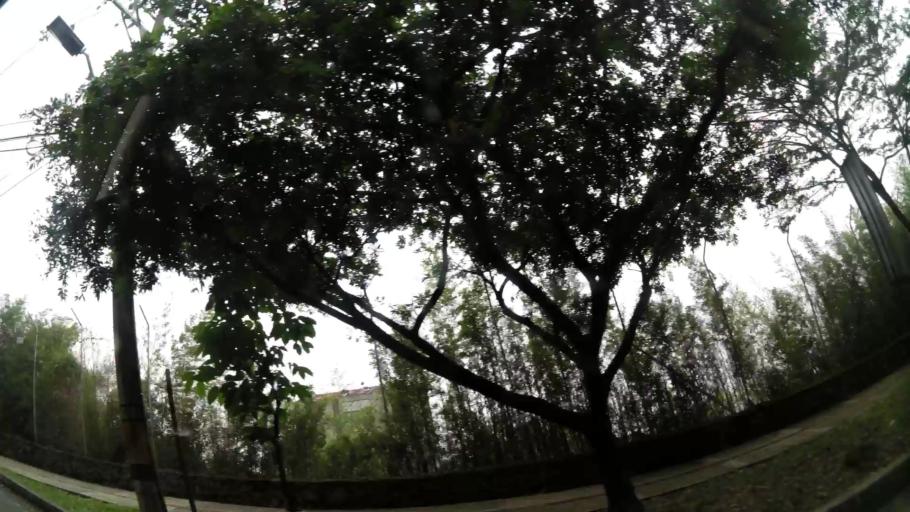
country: CO
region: Antioquia
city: Envigado
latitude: 6.2008
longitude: -75.5597
